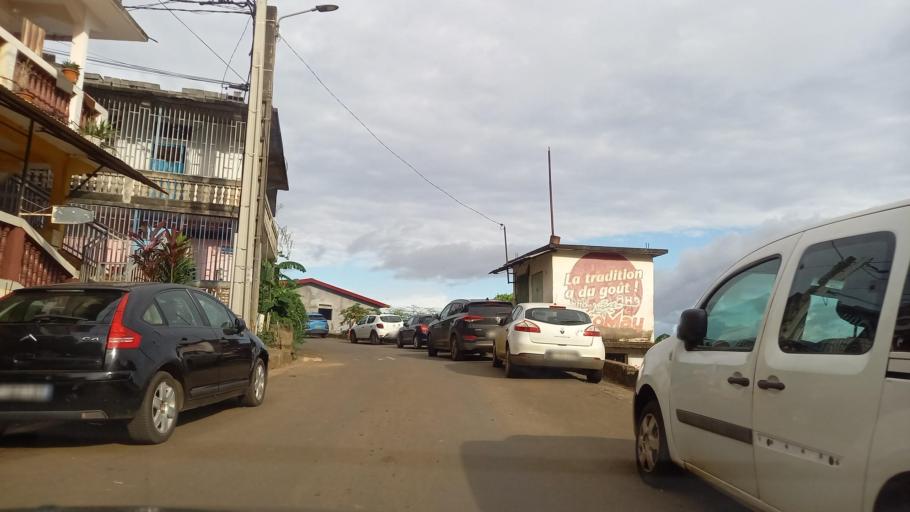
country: YT
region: Sada
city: Sada
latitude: -12.8520
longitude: 45.0993
